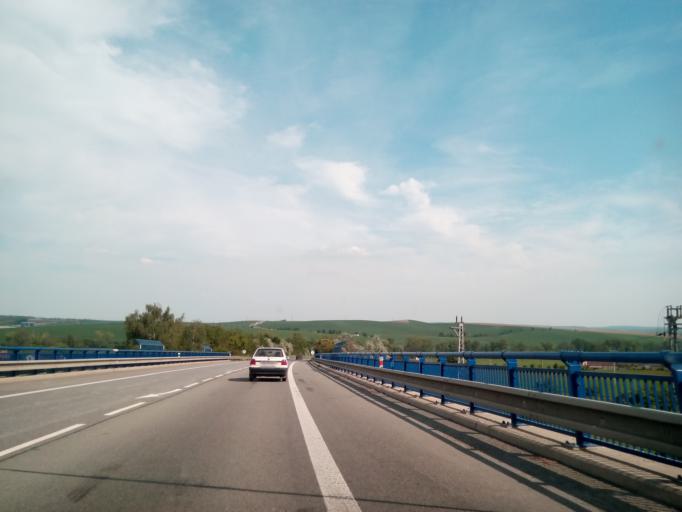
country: CZ
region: South Moravian
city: Blazovice
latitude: 49.1779
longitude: 16.8196
